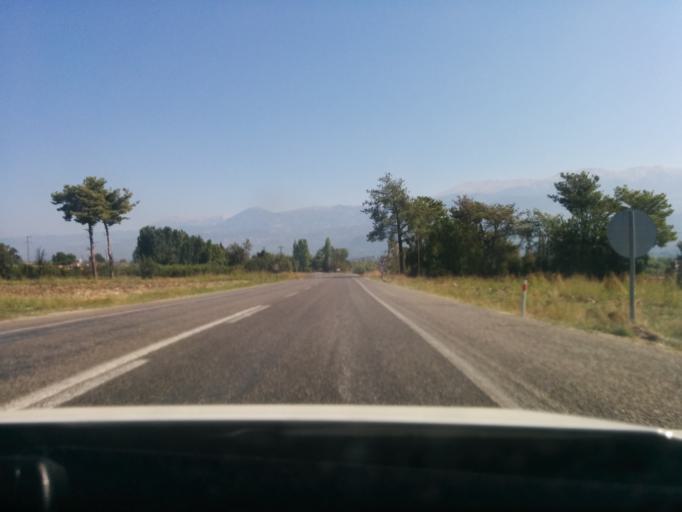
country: TR
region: Mugla
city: Esen
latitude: 36.5055
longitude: 29.3288
